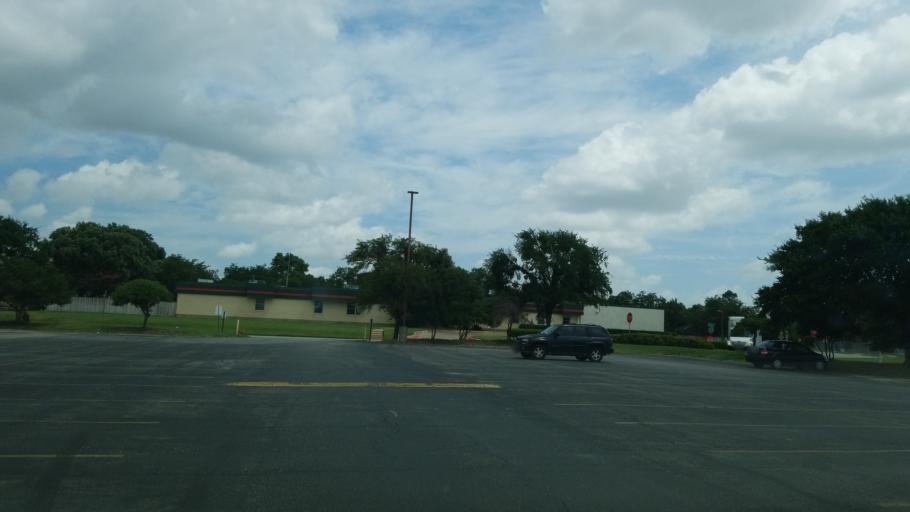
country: US
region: Texas
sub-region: Dallas County
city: Farmers Branch
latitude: 32.8859
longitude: -96.8791
